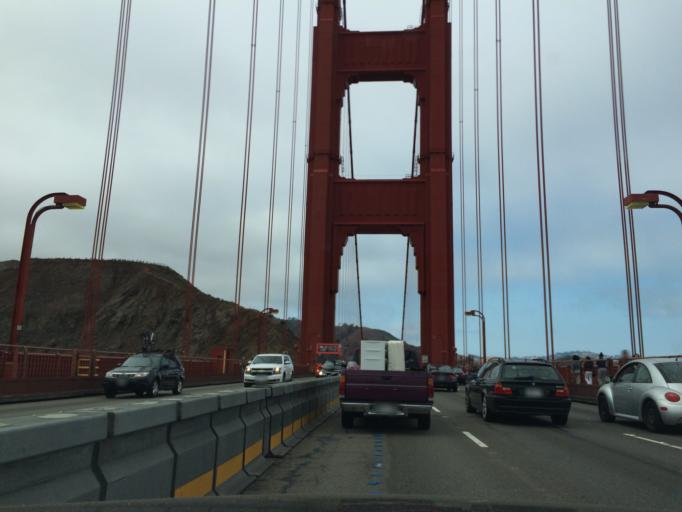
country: US
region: California
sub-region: Marin County
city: Sausalito
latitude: 37.8242
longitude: -122.4790
